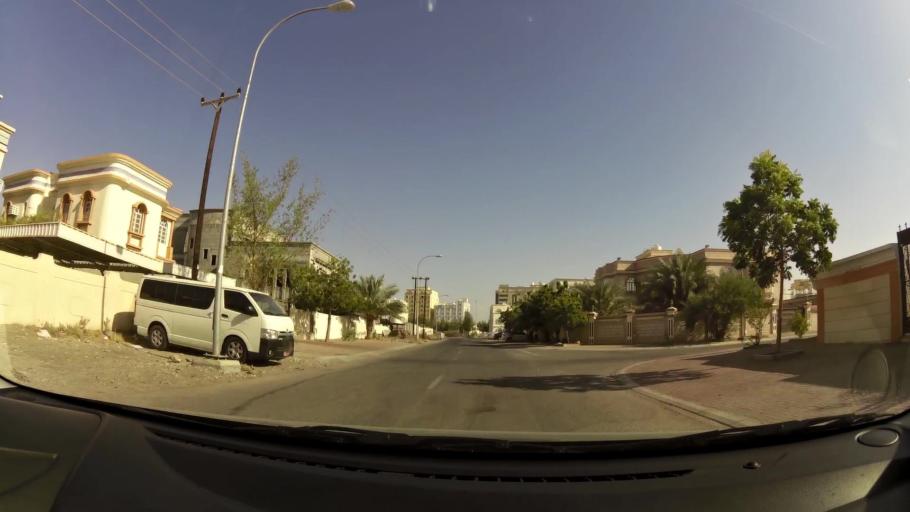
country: OM
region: Muhafazat Masqat
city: As Sib al Jadidah
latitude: 23.6183
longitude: 58.2021
